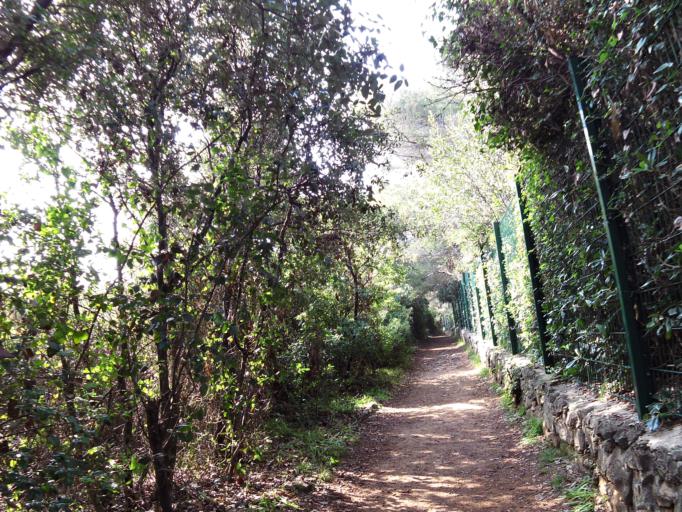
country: FR
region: Provence-Alpes-Cote d'Azur
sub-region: Departement des Alpes-Maritimes
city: Antibes
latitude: 43.5448
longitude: 7.1312
